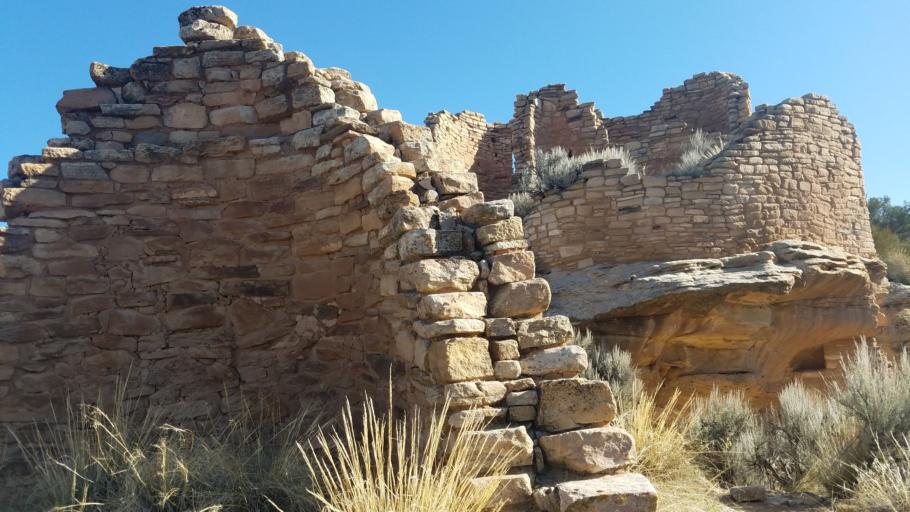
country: US
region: Colorado
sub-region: Dolores County
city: Dove Creek
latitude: 37.4427
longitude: -108.9828
